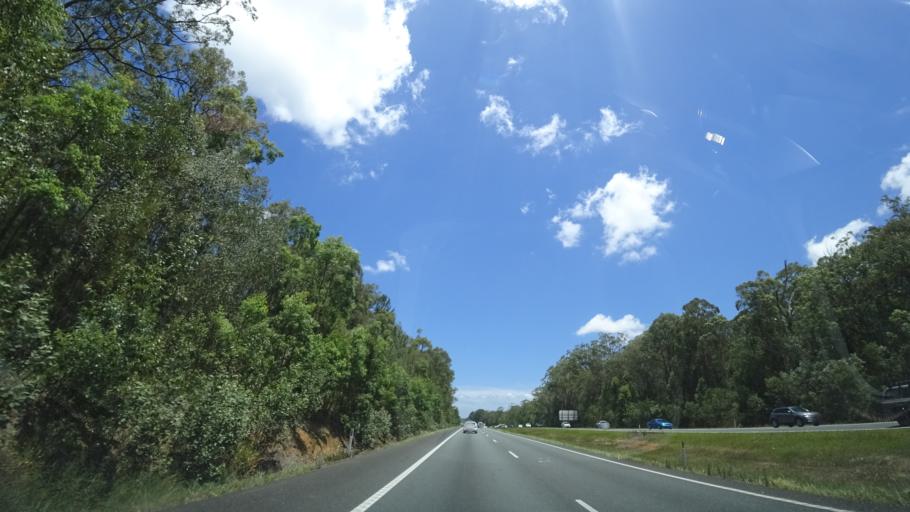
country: AU
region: Queensland
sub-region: Moreton Bay
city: Caboolture
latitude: -27.0091
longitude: 152.9772
